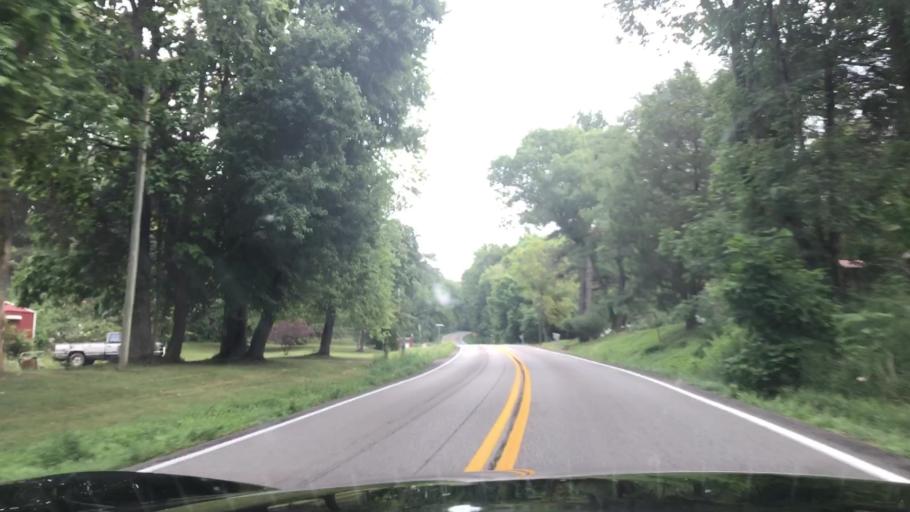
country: US
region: Kentucky
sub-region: Muhlenberg County
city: Central City
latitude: 37.1987
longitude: -87.0309
